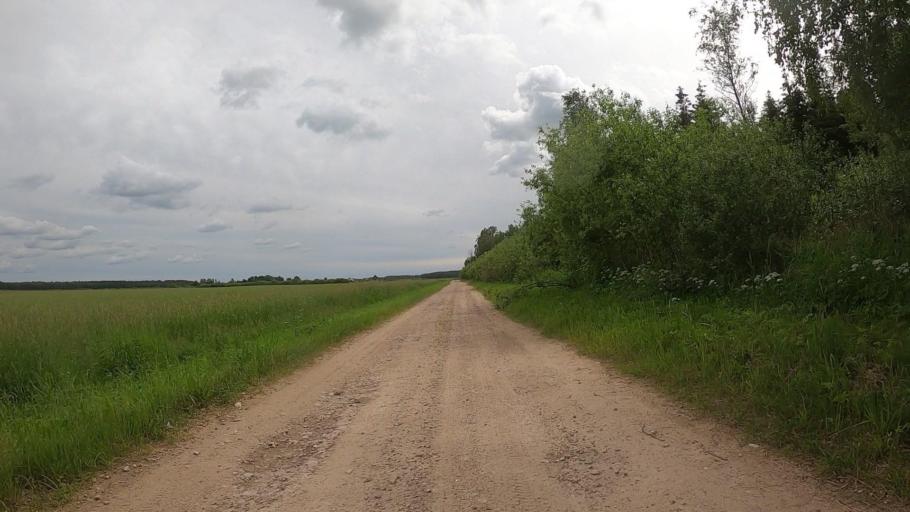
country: LV
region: Olaine
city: Olaine
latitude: 56.8198
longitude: 23.9373
